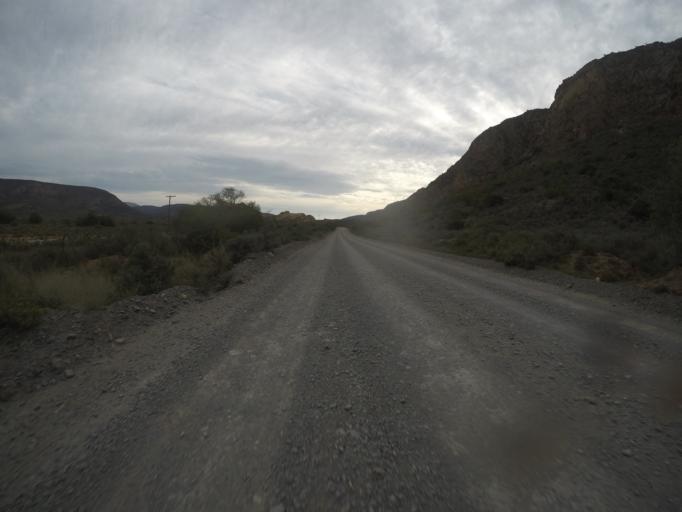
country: ZA
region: Eastern Cape
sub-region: Cacadu District Municipality
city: Willowmore
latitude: -33.5196
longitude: 23.6845
